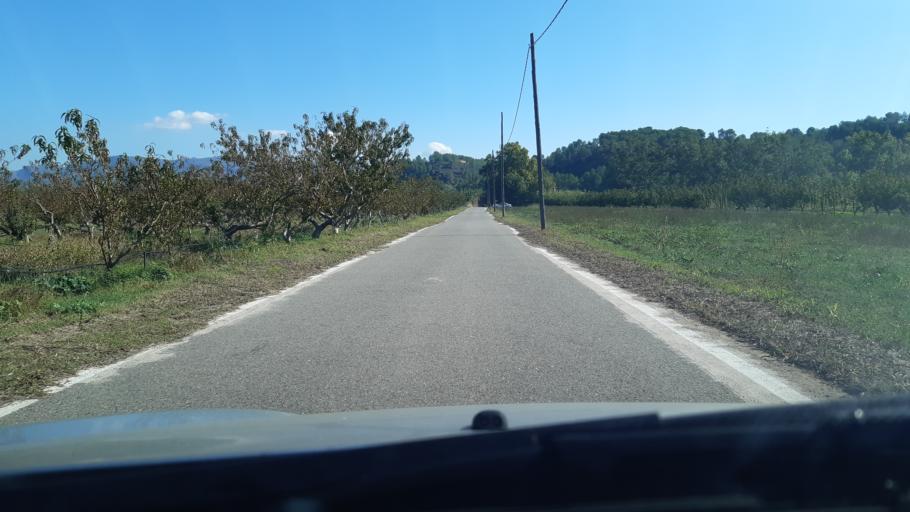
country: ES
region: Catalonia
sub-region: Provincia de Tarragona
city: Miravet
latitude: 41.0342
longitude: 0.6057
